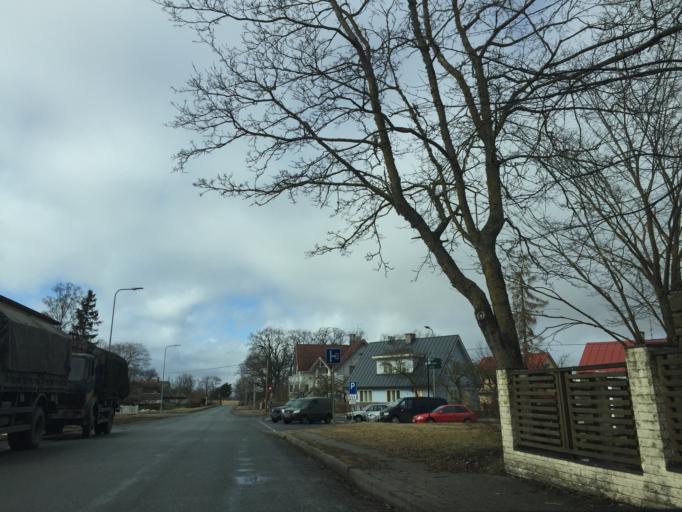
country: EE
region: Laeaene
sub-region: Haapsalu linn
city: Haapsalu
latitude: 58.9479
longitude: 23.5298
